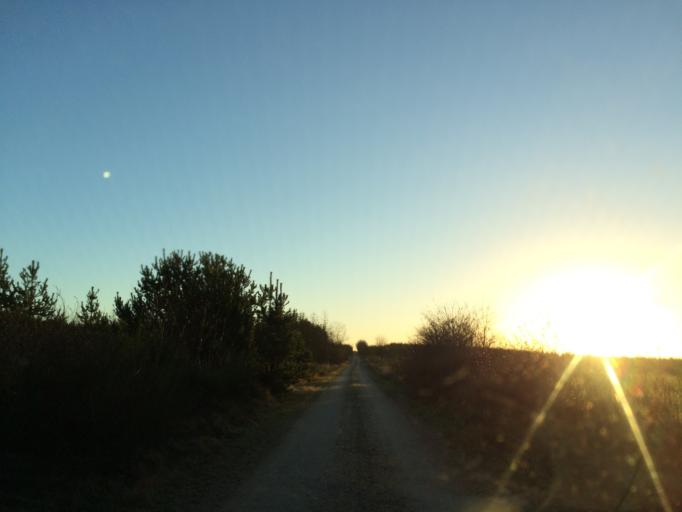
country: DK
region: Central Jutland
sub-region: Holstebro Kommune
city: Holstebro
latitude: 56.2230
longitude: 8.5039
